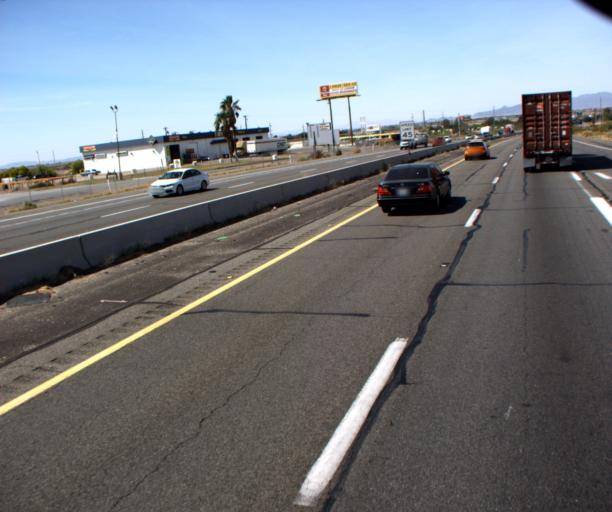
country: US
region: Arizona
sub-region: La Paz County
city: Ehrenberg
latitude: 33.6031
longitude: -114.5233
